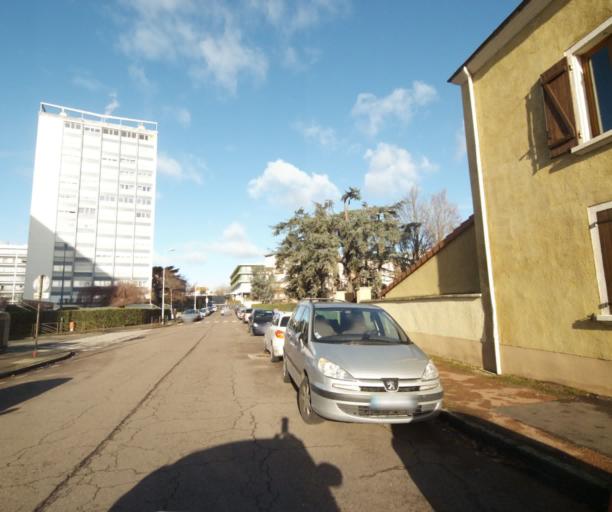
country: FR
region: Rhone-Alpes
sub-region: Departement de la Loire
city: Roanne
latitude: 46.0406
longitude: 4.0793
